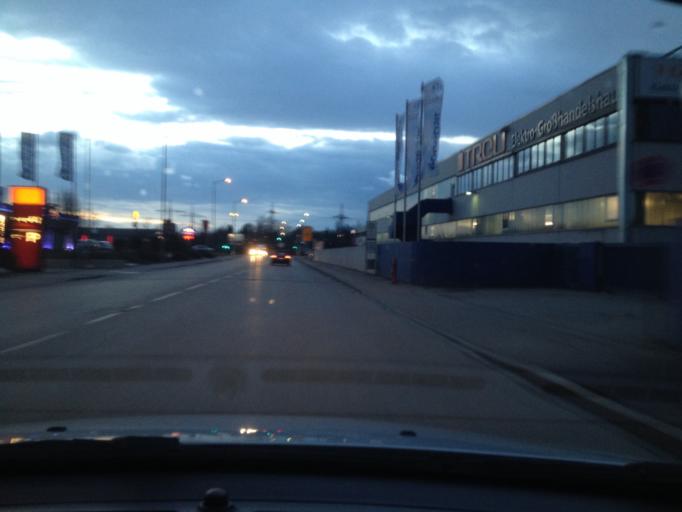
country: DE
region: Bavaria
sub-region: Swabia
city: Gersthofen
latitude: 48.3987
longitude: 10.8741
